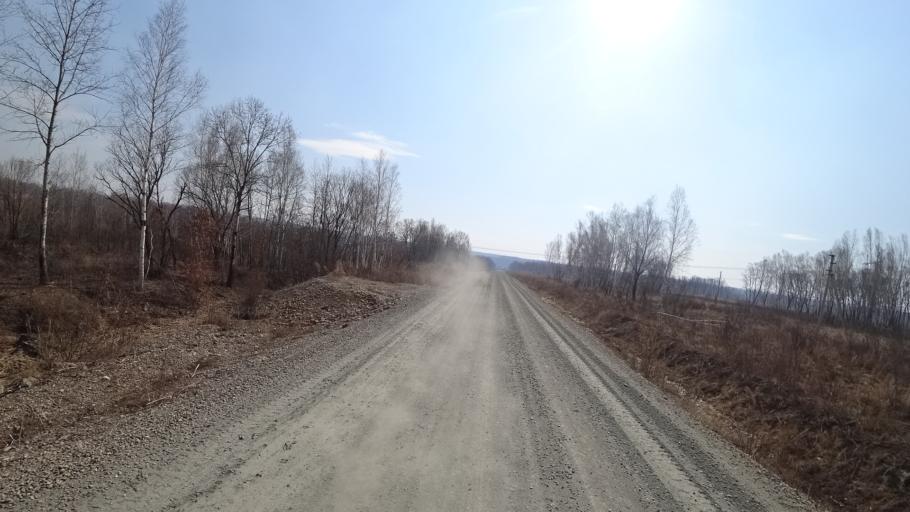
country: RU
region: Amur
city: Novobureyskiy
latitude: 49.8049
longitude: 129.9635
